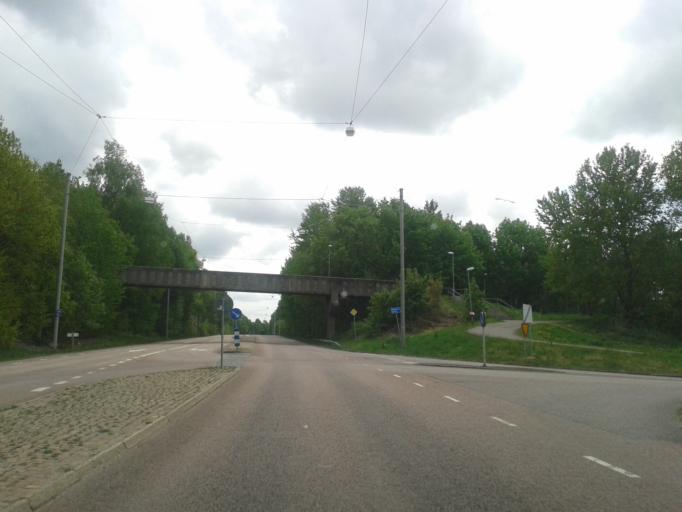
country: SE
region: Vaestra Goetaland
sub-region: Goteborg
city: Gardsten
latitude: 57.8038
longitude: 12.0334
